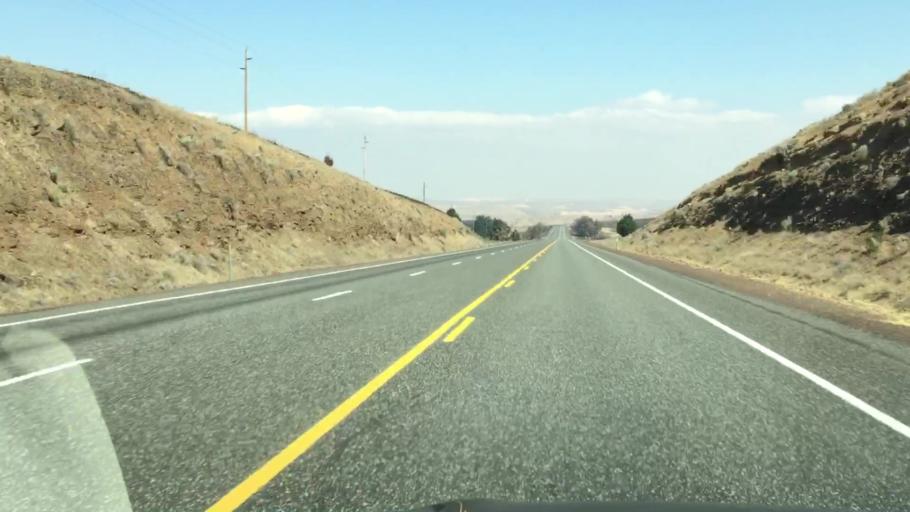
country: US
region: Oregon
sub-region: Wasco County
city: The Dalles
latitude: 45.3763
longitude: -121.1420
